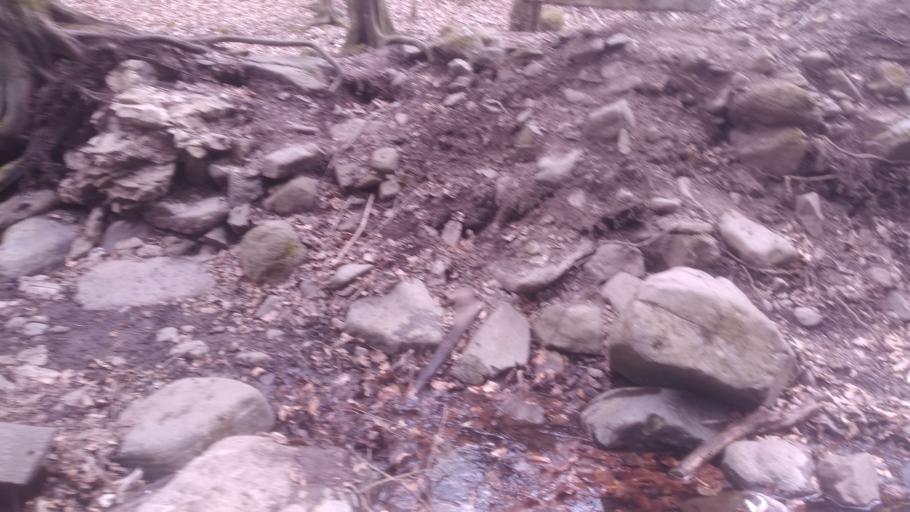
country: SK
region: Nitriansky
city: Sahy
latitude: 47.9746
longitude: 18.8953
